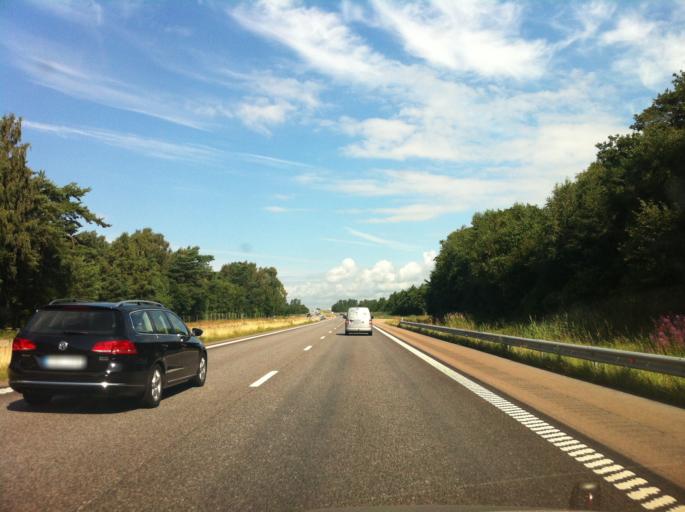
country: SE
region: Halland
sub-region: Halmstads Kommun
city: Paarp
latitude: 56.5894
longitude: 12.9415
